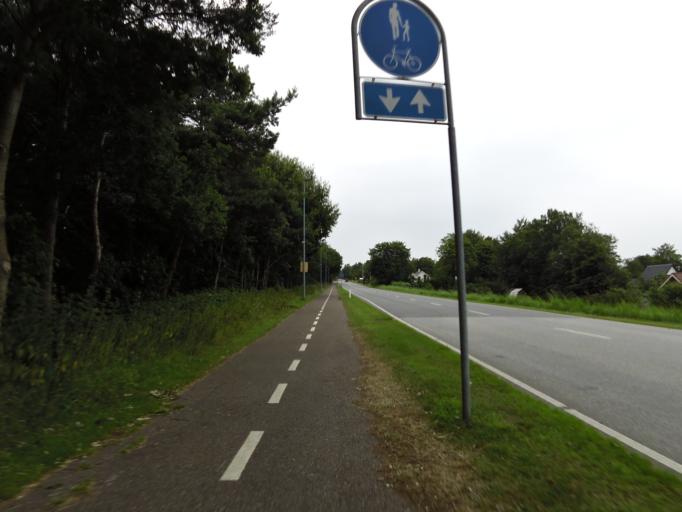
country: DK
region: South Denmark
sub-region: Tonder Kommune
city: Logumkloster
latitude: 55.1526
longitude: 8.9609
